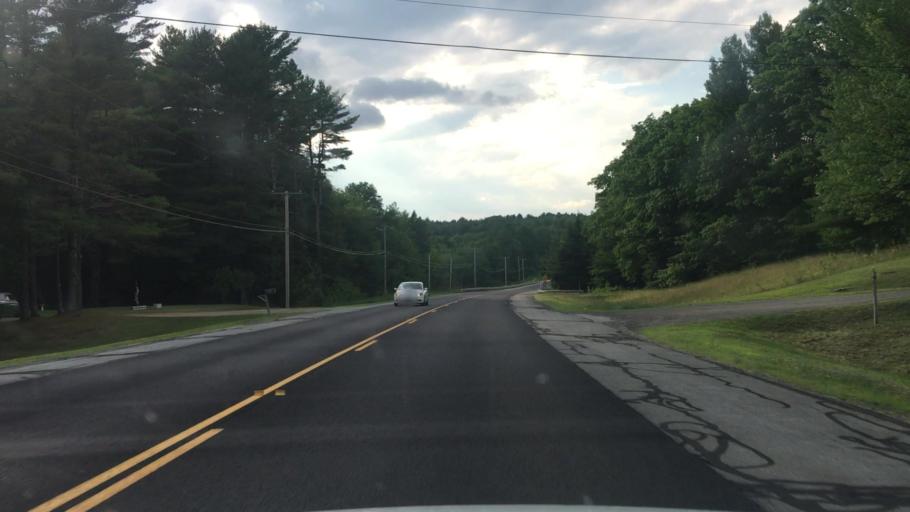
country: US
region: Maine
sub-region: Waldo County
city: Palermo
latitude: 44.3826
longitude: -69.4606
